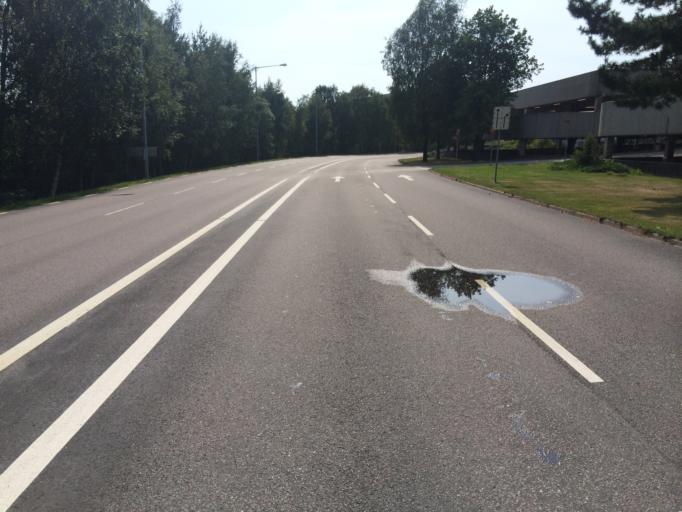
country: SE
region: Vaestra Goetaland
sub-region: Goteborg
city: Majorna
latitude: 57.7271
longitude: 11.8676
